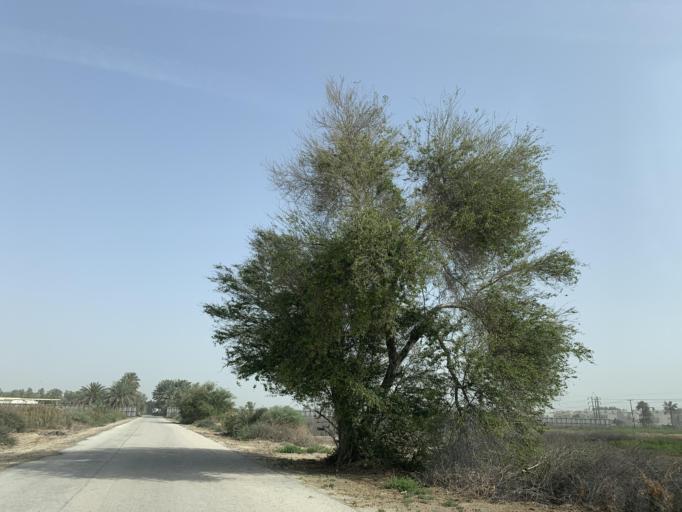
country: BH
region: Northern
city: Madinat `Isa
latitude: 26.1639
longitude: 50.5343
